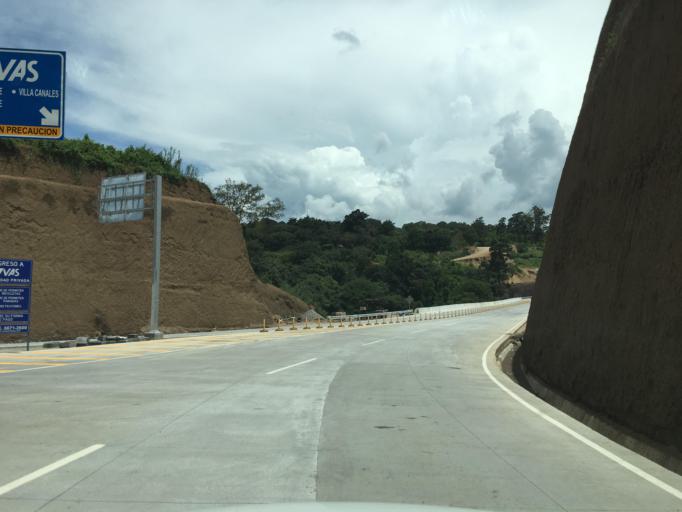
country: GT
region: Guatemala
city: Santa Catarina Pinula
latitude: 14.5745
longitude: -90.5396
